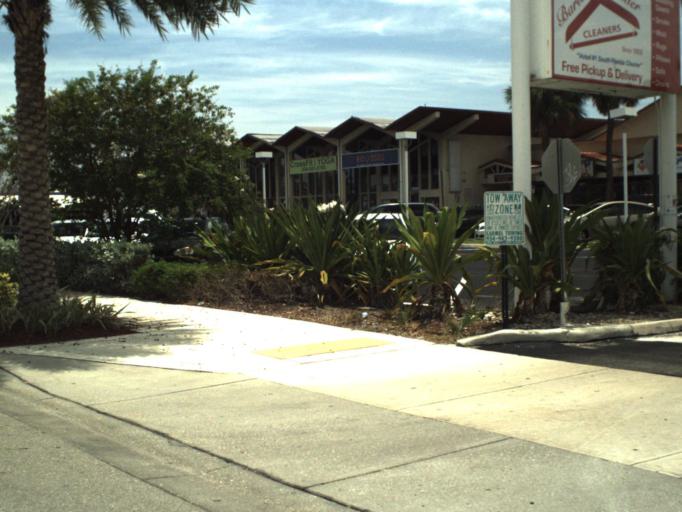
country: US
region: Florida
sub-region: Broward County
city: Terra Mar
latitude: 26.2318
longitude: -80.0966
